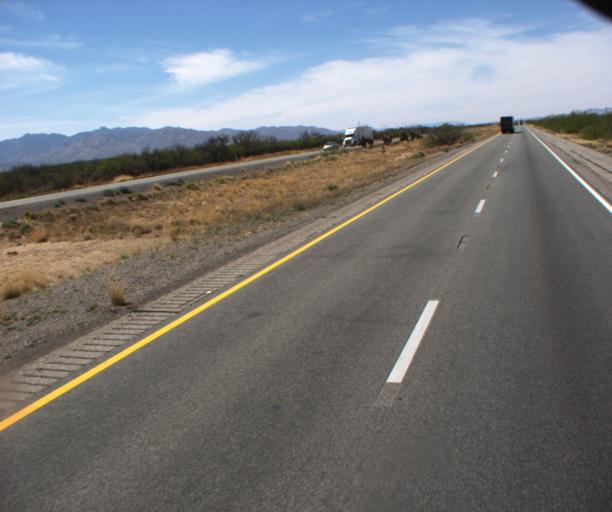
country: US
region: Arizona
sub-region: Cochise County
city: Willcox
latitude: 32.3038
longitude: -109.3817
